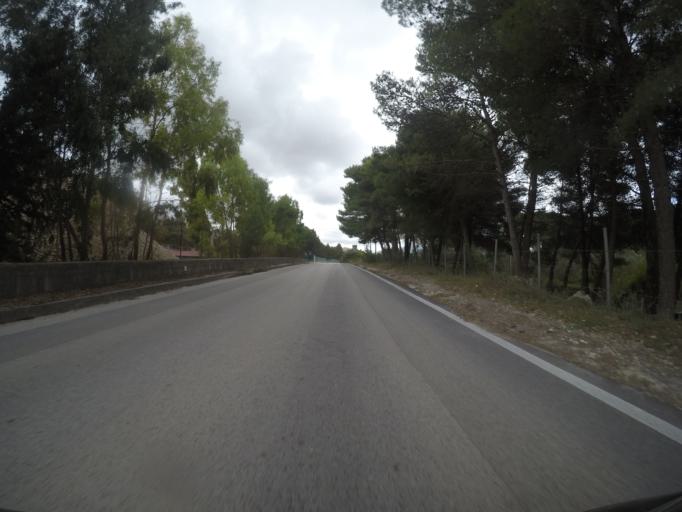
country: IT
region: Sicily
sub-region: Palermo
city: Montelepre
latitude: 38.1059
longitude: 13.1704
